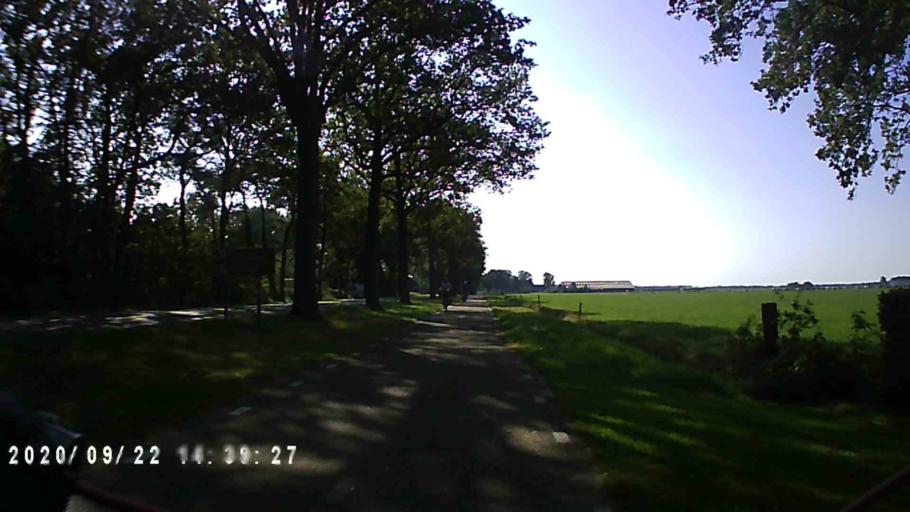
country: NL
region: Groningen
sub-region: Gemeente Leek
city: Leek
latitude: 53.0240
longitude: 6.3497
